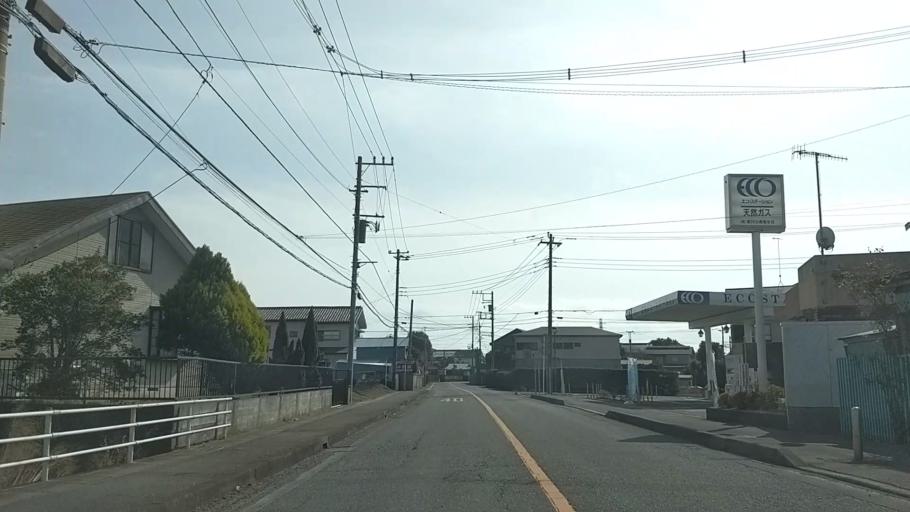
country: JP
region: Kanagawa
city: Chigasaki
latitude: 35.3563
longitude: 139.3844
